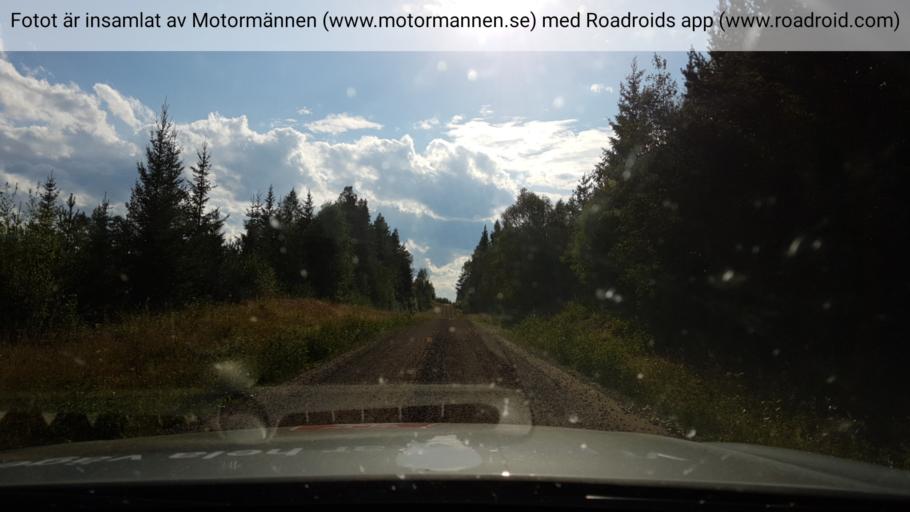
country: SE
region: Jaemtland
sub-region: Stroemsunds Kommun
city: Stroemsund
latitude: 63.7220
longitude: 16.0806
